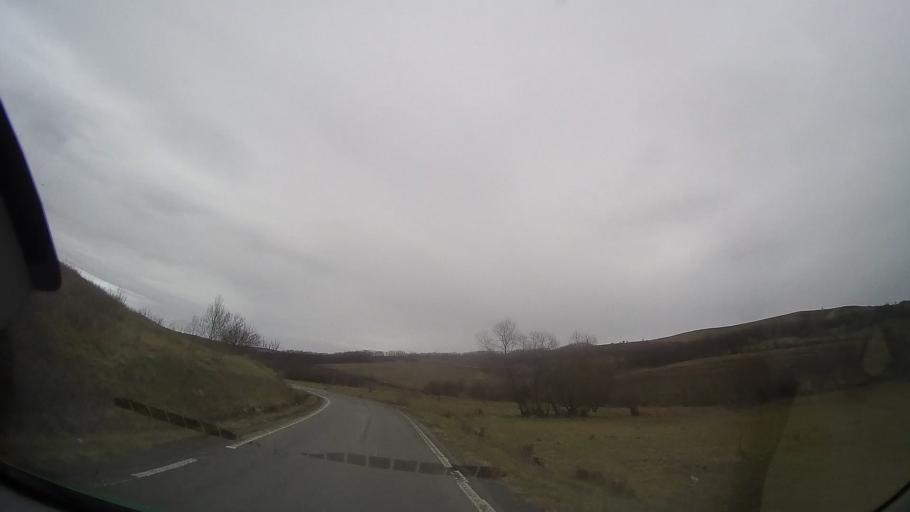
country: RO
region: Mures
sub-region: Comuna Bala
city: Bala
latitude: 46.7140
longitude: 24.5274
